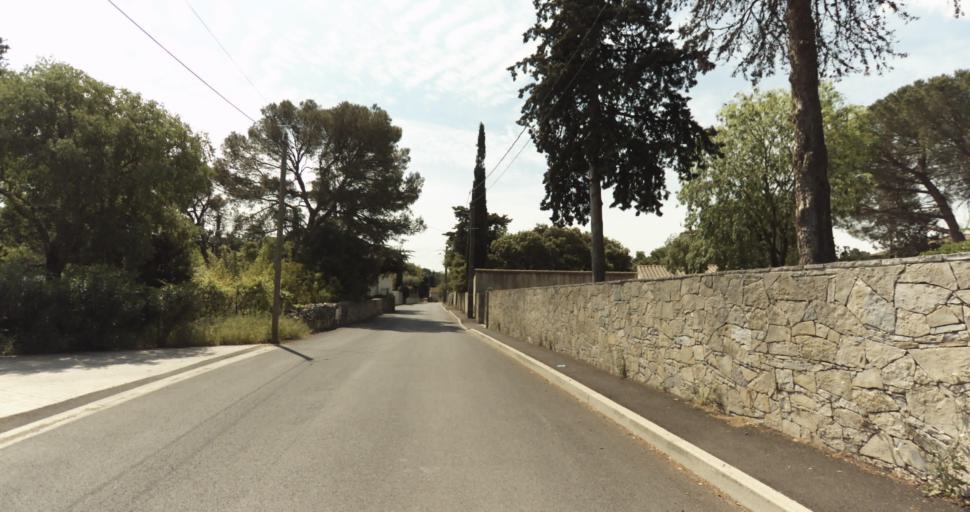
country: FR
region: Languedoc-Roussillon
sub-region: Departement du Gard
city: Nimes
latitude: 43.8562
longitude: 4.3483
